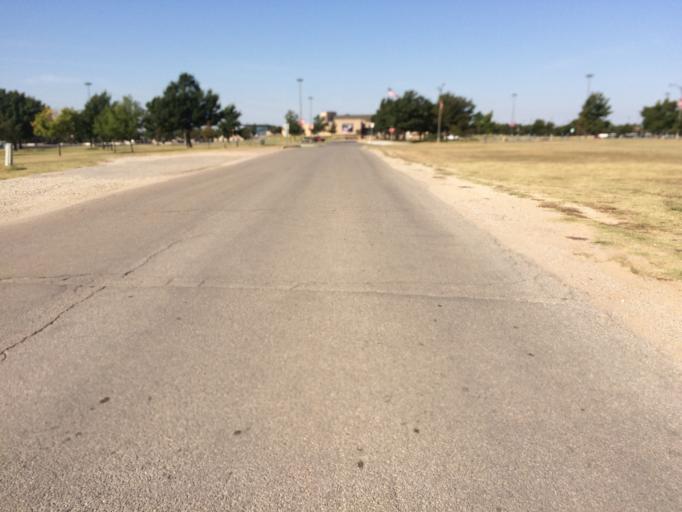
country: US
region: Oklahoma
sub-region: Cleveland County
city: Norman
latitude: 35.1872
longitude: -97.4400
